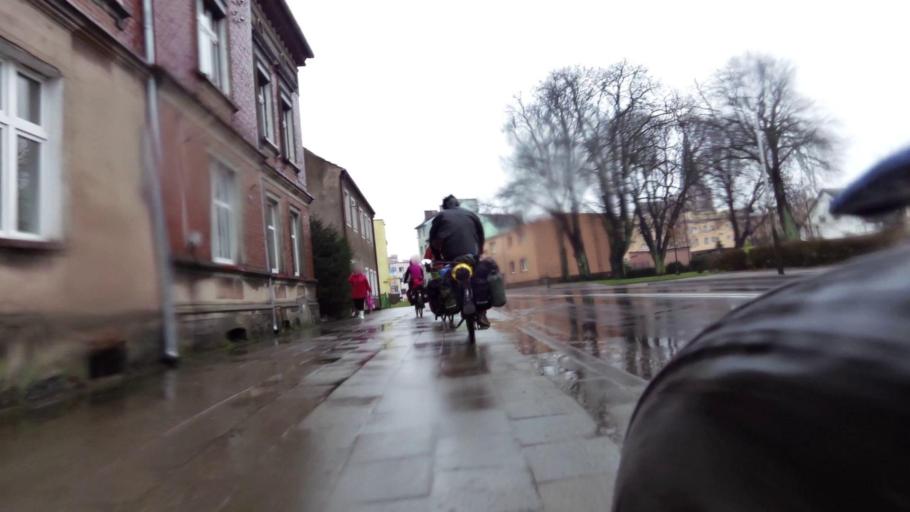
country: PL
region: West Pomeranian Voivodeship
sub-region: Powiat drawski
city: Drawsko Pomorskie
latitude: 53.5338
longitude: 15.8131
